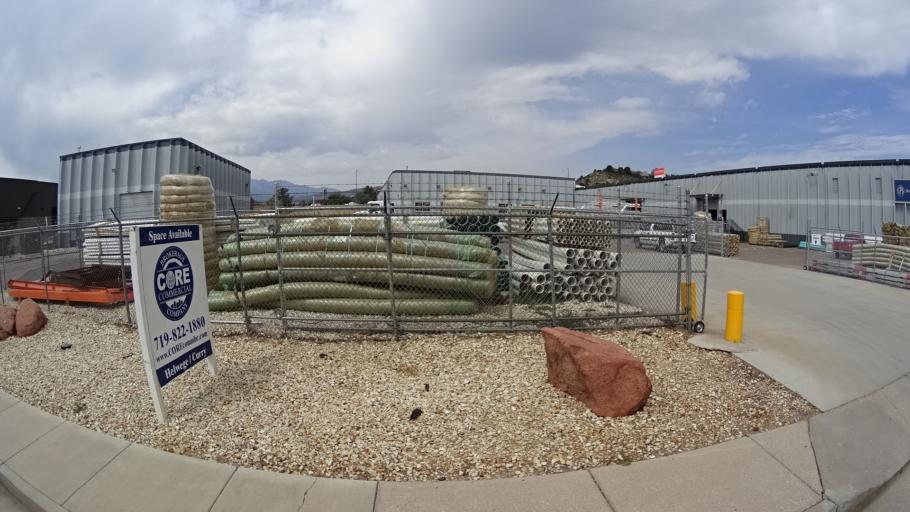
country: US
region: Colorado
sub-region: El Paso County
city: Colorado Springs
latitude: 38.8998
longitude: -104.8267
